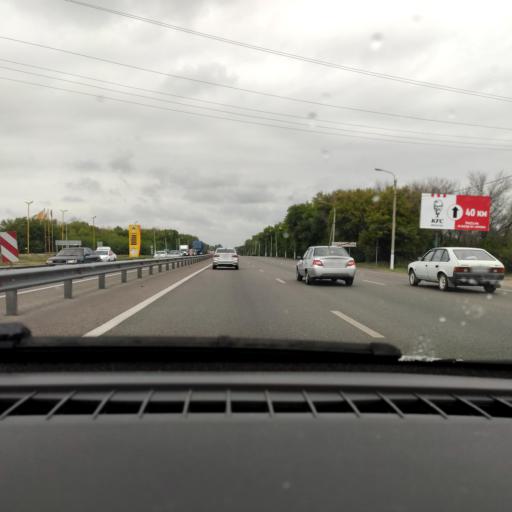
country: RU
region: Voronezj
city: Novaya Usman'
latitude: 51.6195
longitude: 39.3664
